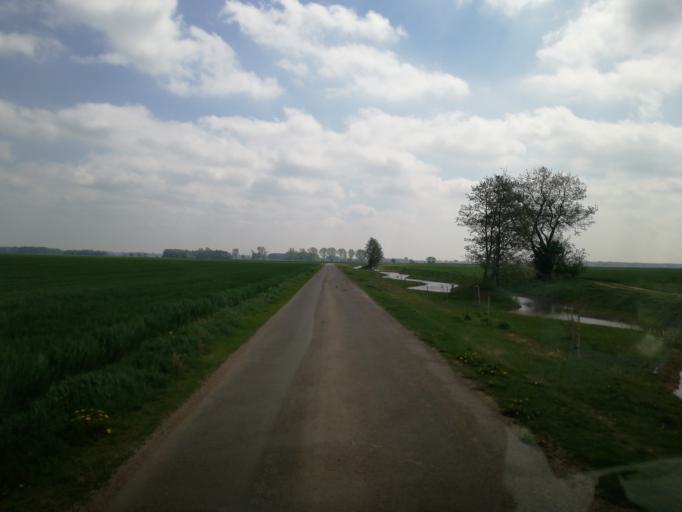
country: DE
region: Brandenburg
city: Doberlug-Kirchhain
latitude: 51.6873
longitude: 13.5316
